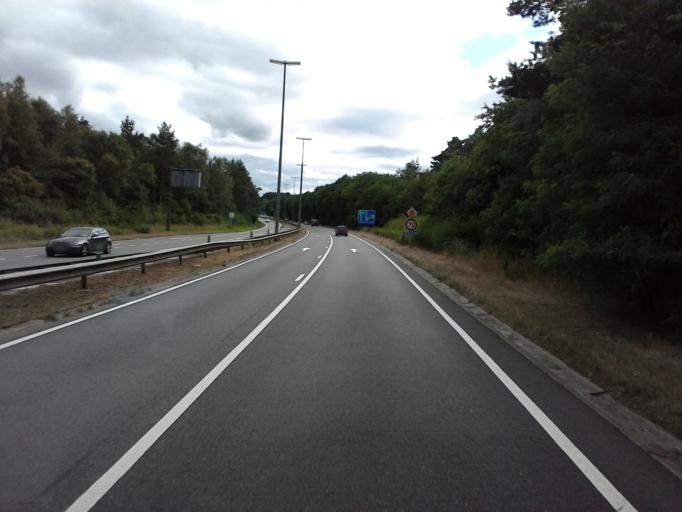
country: BE
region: Wallonia
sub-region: Province du Luxembourg
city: Arlon
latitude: 49.6777
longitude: 5.7808
